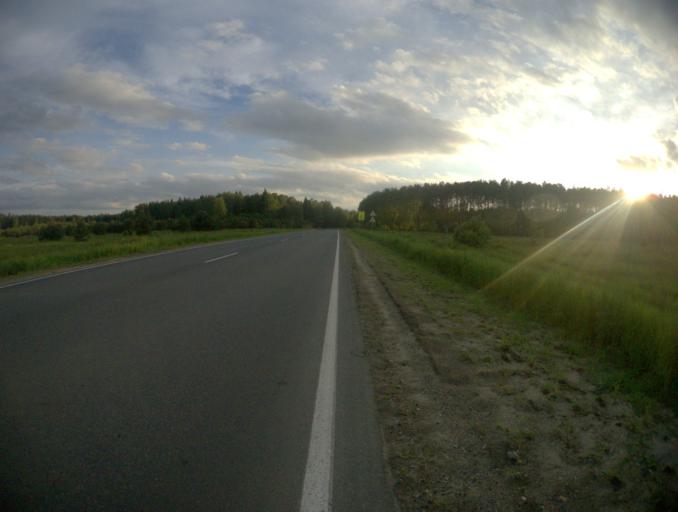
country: RU
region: Vladimir
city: Anopino
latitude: 55.6333
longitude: 40.7953
